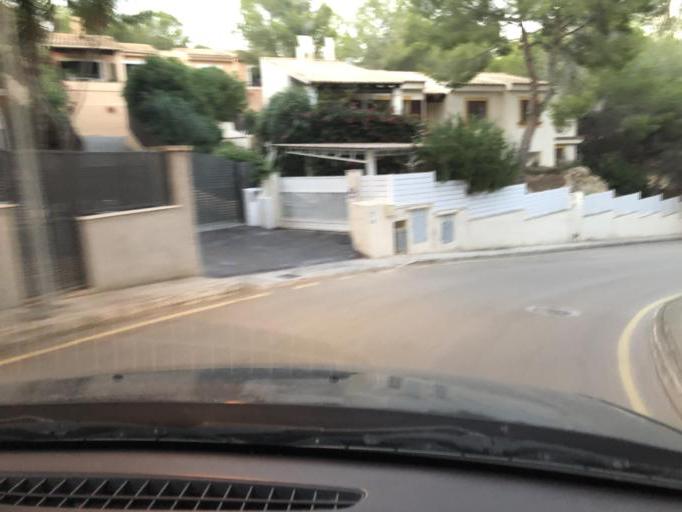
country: ES
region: Balearic Islands
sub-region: Illes Balears
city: Santa Ponsa
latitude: 39.5288
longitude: 2.4748
